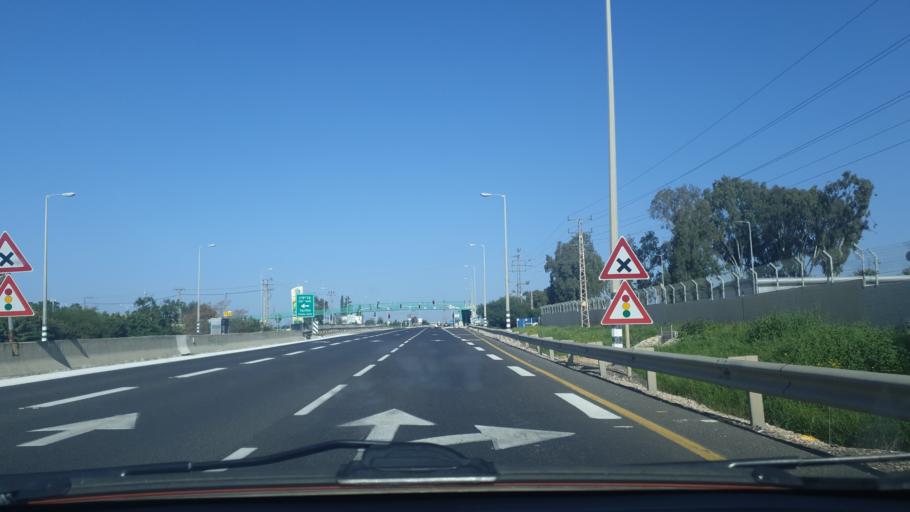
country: IL
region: Central District
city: Kefar Habad
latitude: 31.9680
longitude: 34.8451
